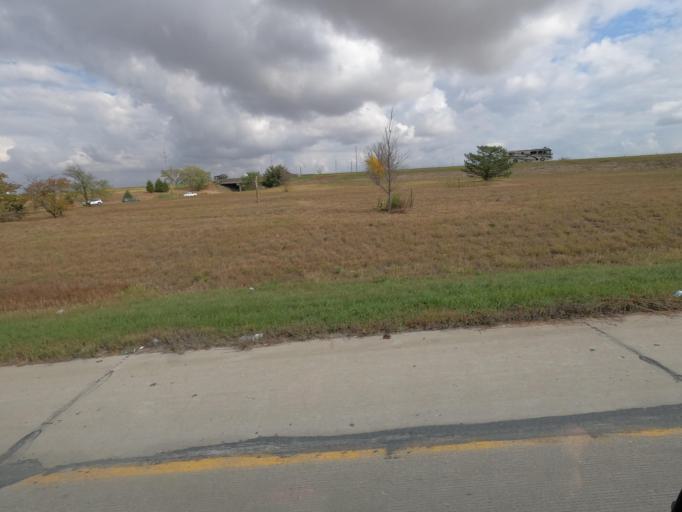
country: US
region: Iowa
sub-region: Story County
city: Ames
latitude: 42.0334
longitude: -93.5723
